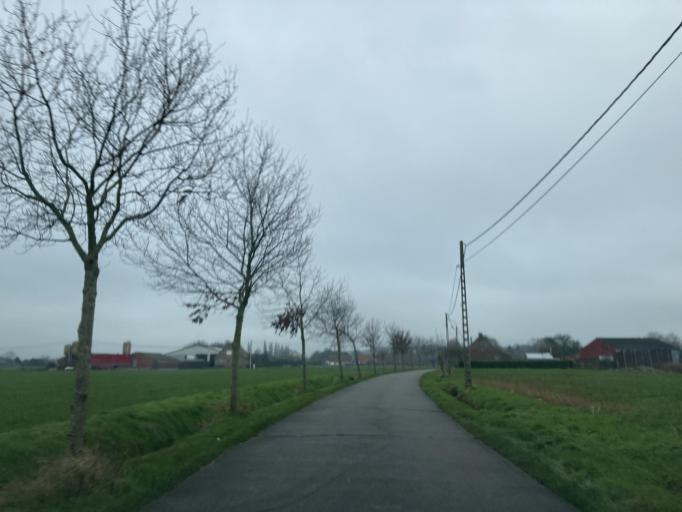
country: BE
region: Flanders
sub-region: Provincie West-Vlaanderen
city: Ichtegem
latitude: 51.1298
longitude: 3.0524
